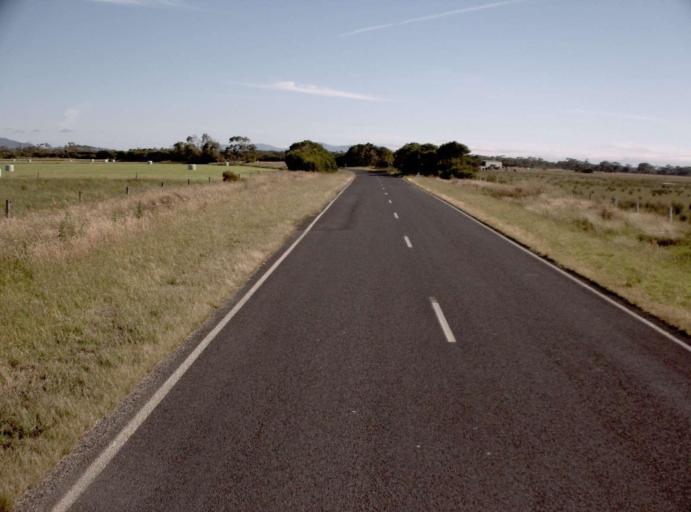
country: AU
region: Victoria
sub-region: Latrobe
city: Morwell
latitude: -38.6869
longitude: 146.3895
